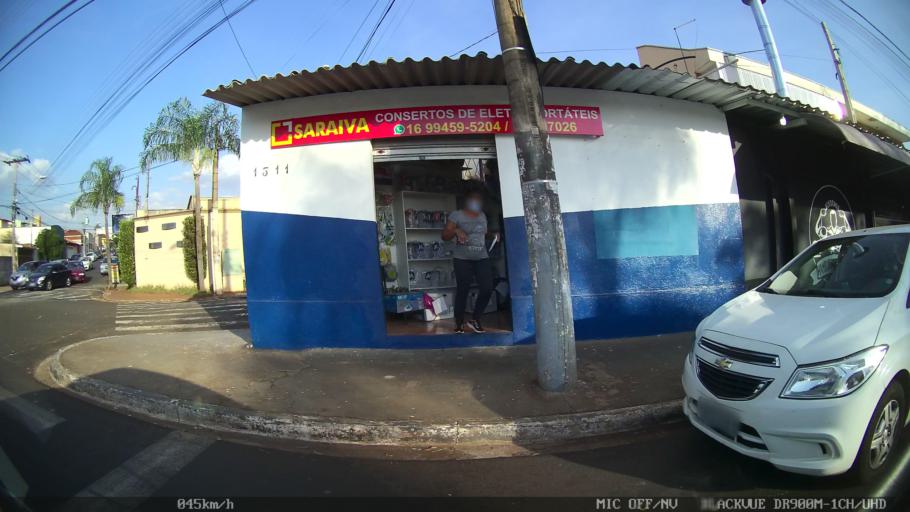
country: BR
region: Sao Paulo
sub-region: Ribeirao Preto
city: Ribeirao Preto
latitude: -21.1662
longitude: -47.8270
